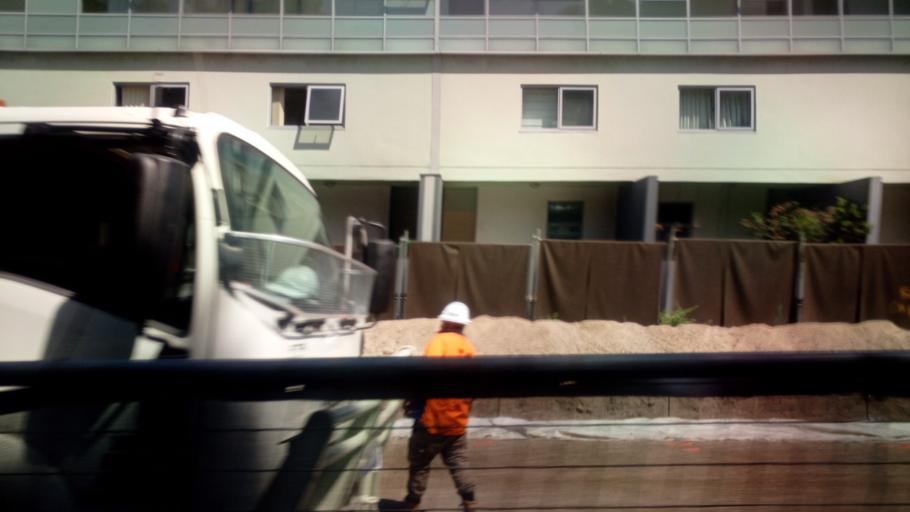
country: AU
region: New South Wales
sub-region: City of Sydney
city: Alexandria
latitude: -33.9067
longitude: 151.1911
